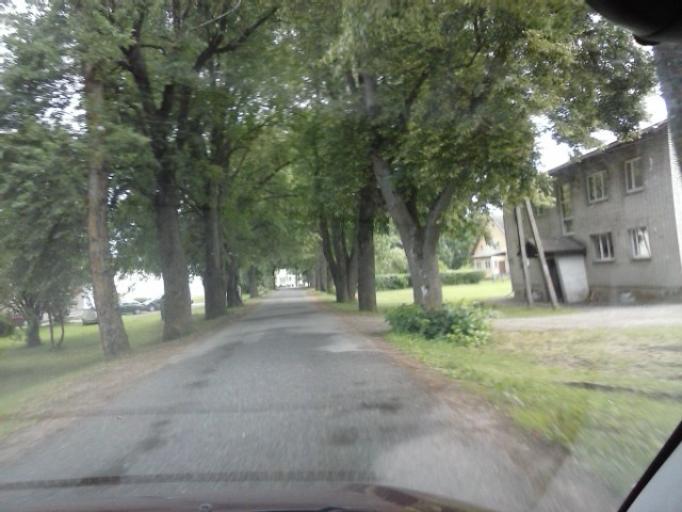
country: EE
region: Tartu
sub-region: Tartu linn
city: Tartu
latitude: 58.3559
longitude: 26.8760
